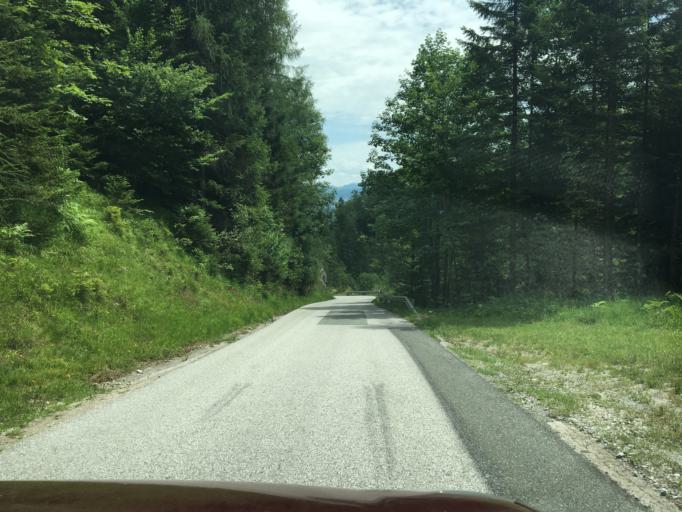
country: AT
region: Salzburg
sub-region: Politischer Bezirk Hallein
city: Scheffau am Tennengebirge
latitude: 47.6007
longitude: 13.2865
